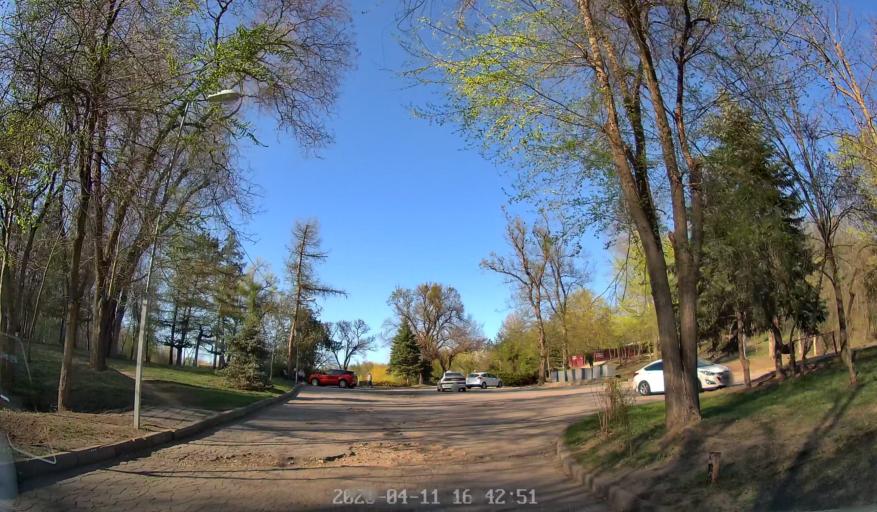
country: MD
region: Chisinau
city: Chisinau
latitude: 47.0372
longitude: 28.8707
